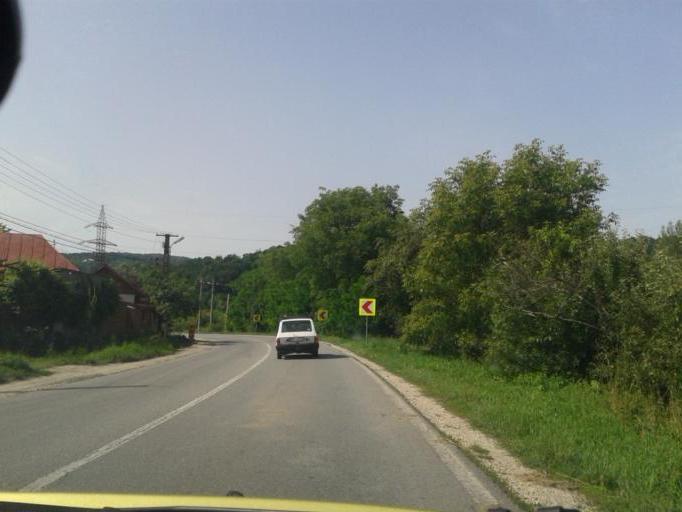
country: RO
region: Valcea
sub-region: Oras Baile Govora
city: Baile Govora
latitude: 45.0717
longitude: 24.2226
